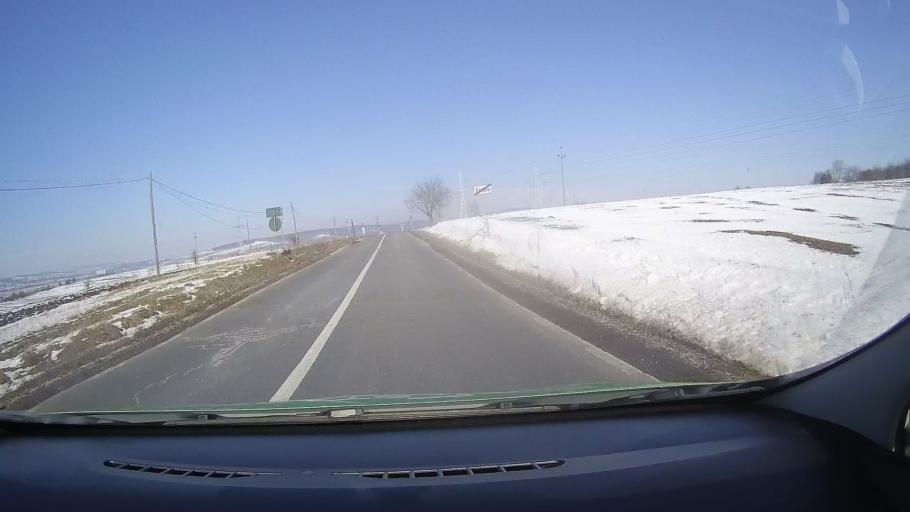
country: RO
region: Brasov
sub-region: Comuna Hoghiz
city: Hoghiz
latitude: 45.9718
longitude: 25.3020
